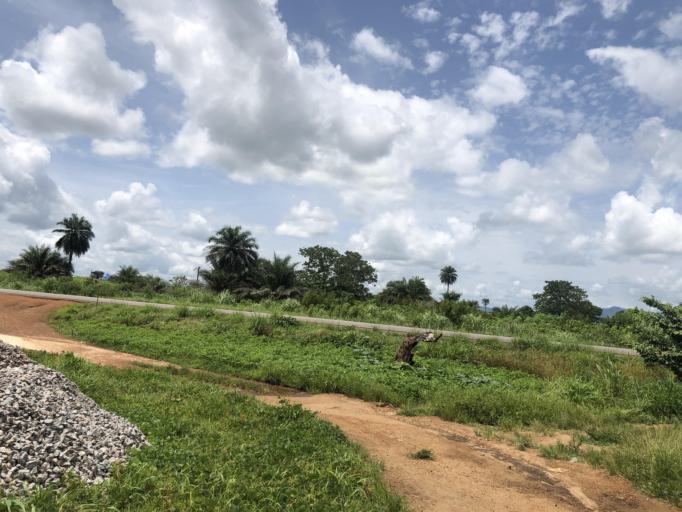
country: SL
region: Northern Province
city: Magburaka
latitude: 8.7017
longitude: -11.9247
